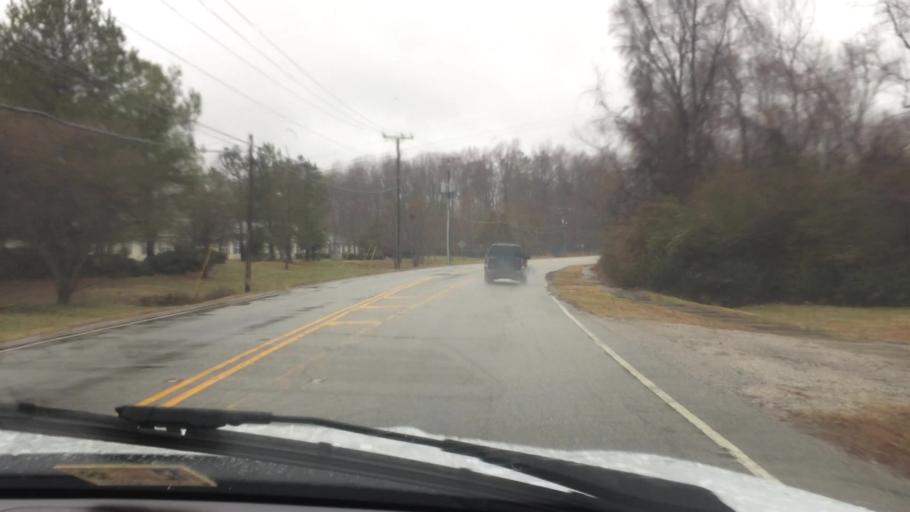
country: US
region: Virginia
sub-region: City of Williamsburg
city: Williamsburg
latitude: 37.2193
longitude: -76.6250
